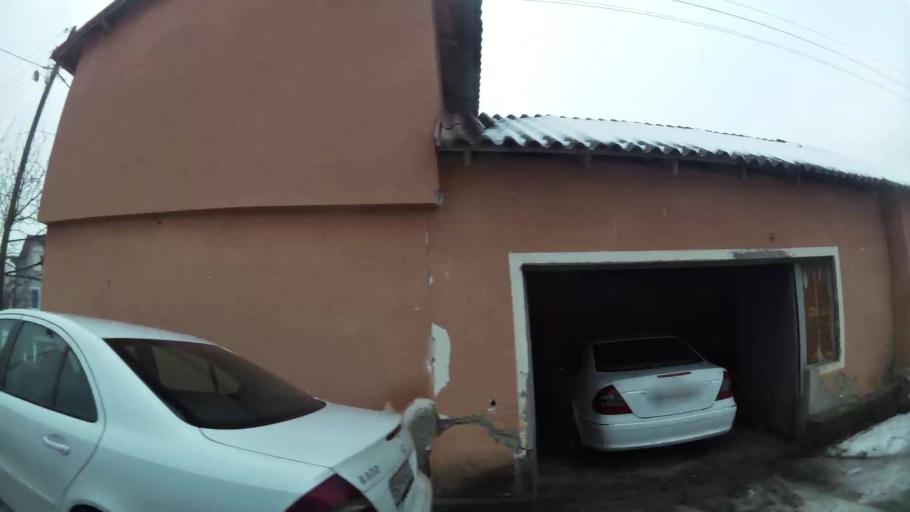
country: MK
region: Petrovec
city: Petrovec
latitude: 41.9356
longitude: 21.6108
